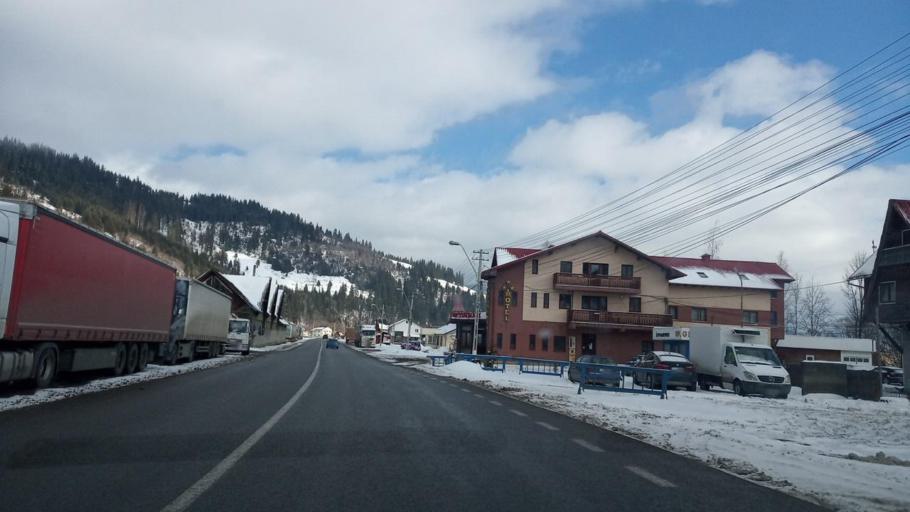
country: RO
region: Suceava
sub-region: Municipiul Vatra Dornei
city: Vatra Dornei
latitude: 47.3469
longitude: 25.3238
